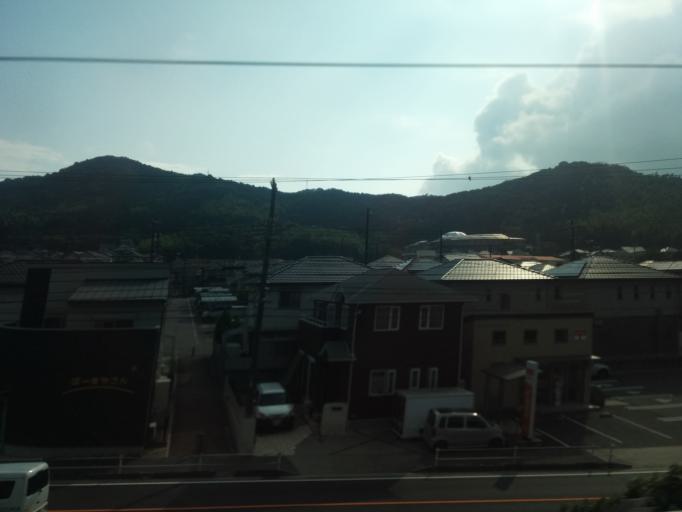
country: JP
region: Aichi
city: Gamagori
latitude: 34.8644
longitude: 137.1566
